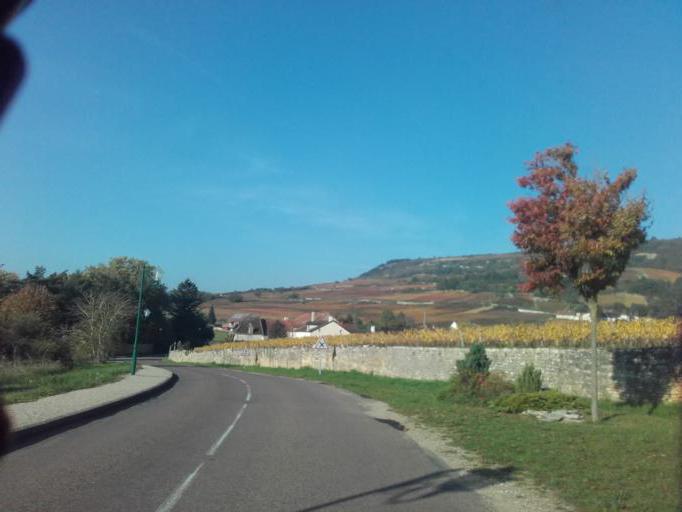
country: FR
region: Bourgogne
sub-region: Departement de Saone-et-Loire
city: Chagny
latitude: 46.9104
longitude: 4.6859
